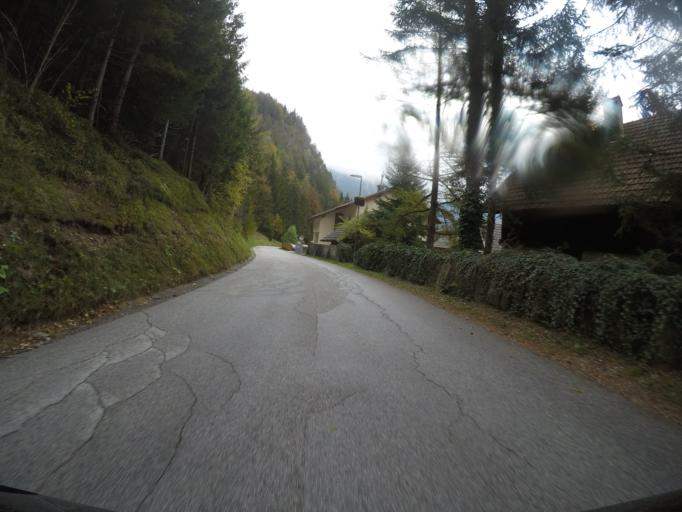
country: SI
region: Kranjska Gora
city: Mojstrana
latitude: 46.4555
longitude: 13.9324
